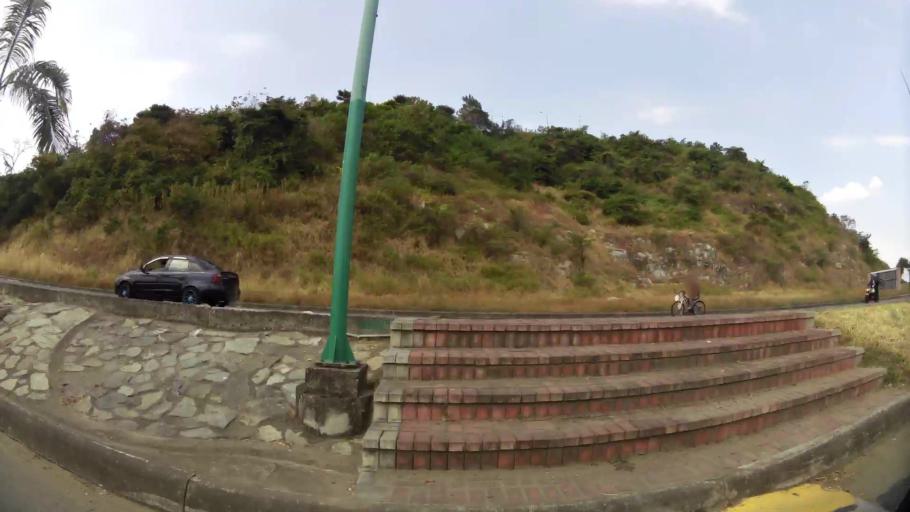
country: EC
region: Guayas
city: El Triunfo
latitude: -2.0377
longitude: -79.9155
